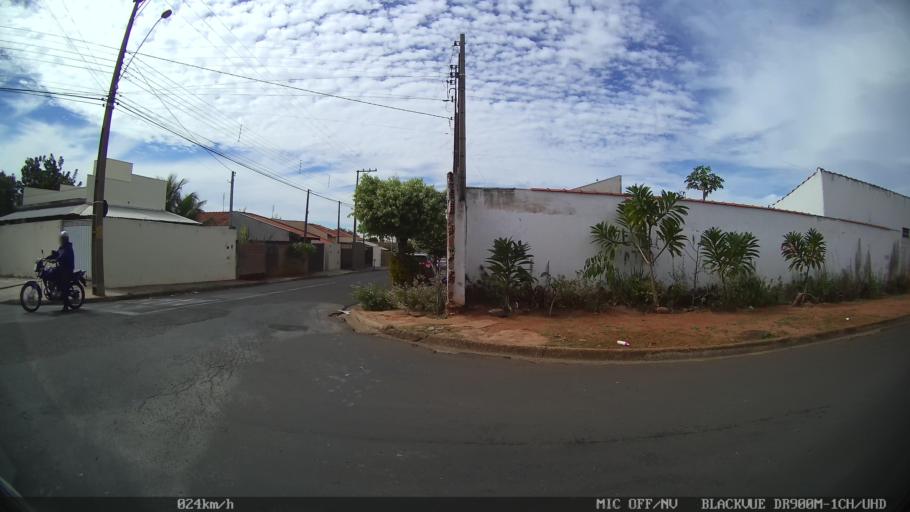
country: BR
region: Sao Paulo
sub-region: Catanduva
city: Catanduva
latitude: -21.1601
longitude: -48.9701
